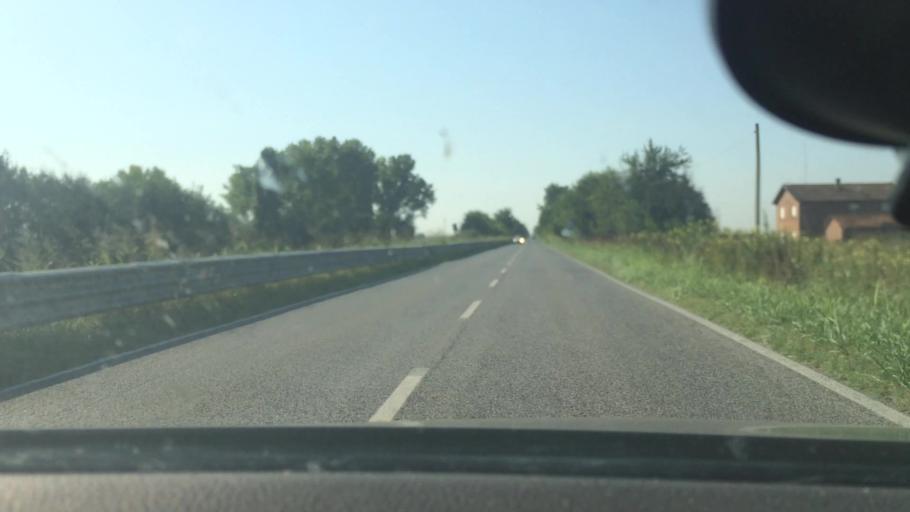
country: IT
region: Emilia-Romagna
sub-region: Provincia di Ferrara
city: Lagosanto
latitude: 44.7413
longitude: 12.1433
